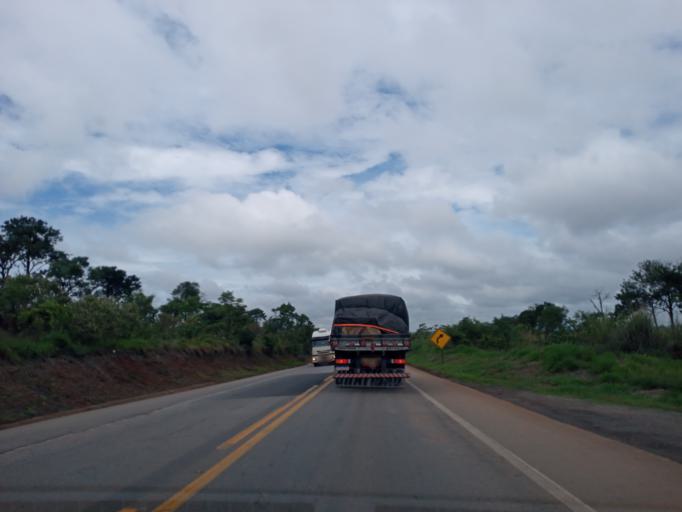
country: BR
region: Minas Gerais
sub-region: Ibia
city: Ibia
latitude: -19.5875
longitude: -46.3591
